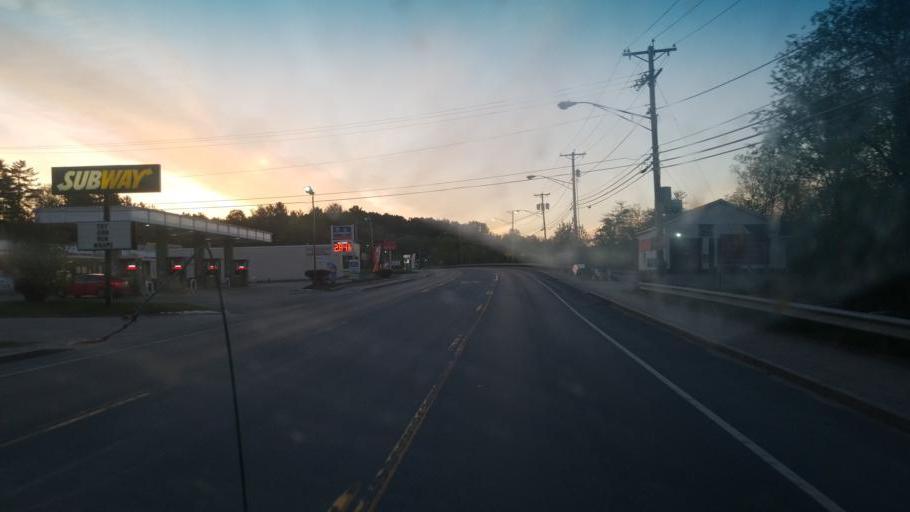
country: US
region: New Hampshire
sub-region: Grafton County
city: Littleton
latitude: 44.3086
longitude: -71.7927
